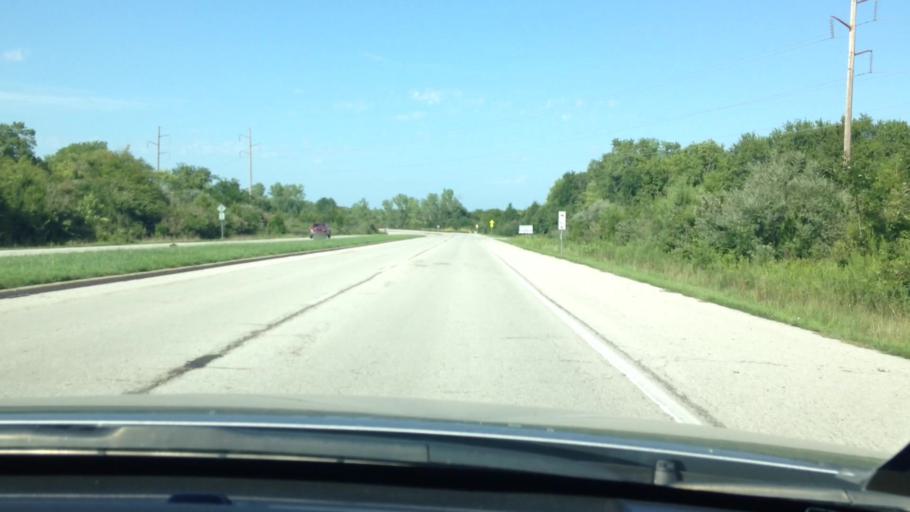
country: US
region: Missouri
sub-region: Jackson County
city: Grandview
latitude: 38.9056
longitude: -94.4852
